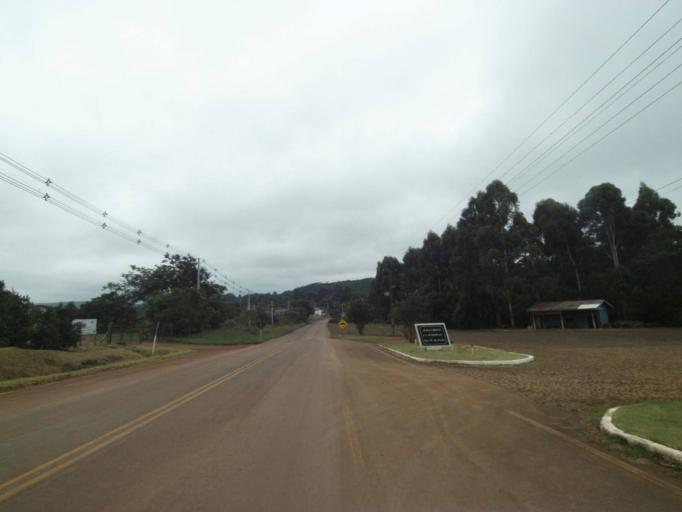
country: BR
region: Parana
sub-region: Pitanga
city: Pitanga
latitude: -24.9281
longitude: -51.8744
